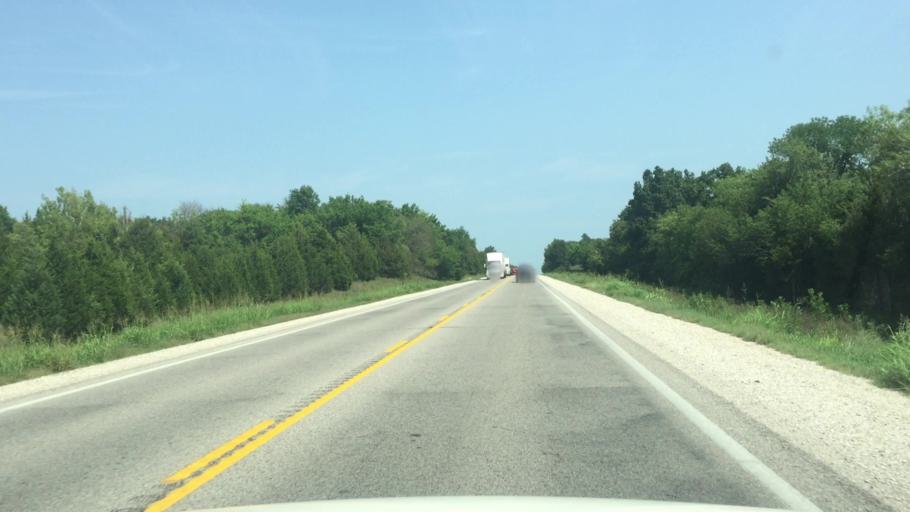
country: US
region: Kansas
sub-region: Montgomery County
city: Coffeyville
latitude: 37.1460
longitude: -95.5768
